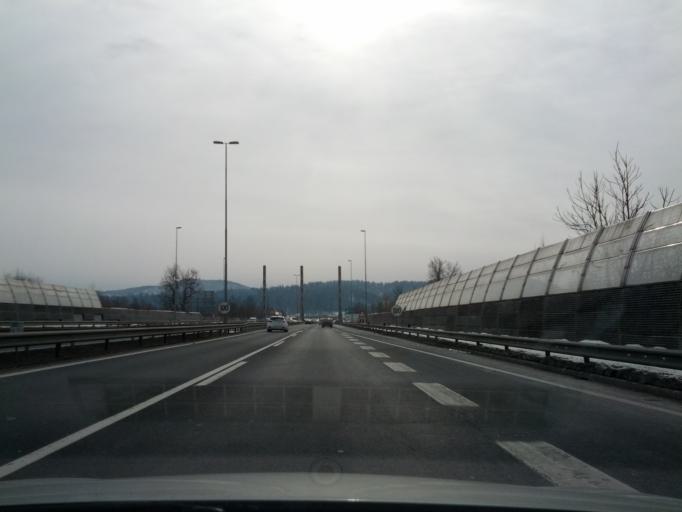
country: SI
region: Dol pri Ljubljani
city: Dol pri Ljubljani
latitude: 46.0508
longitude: 14.5746
